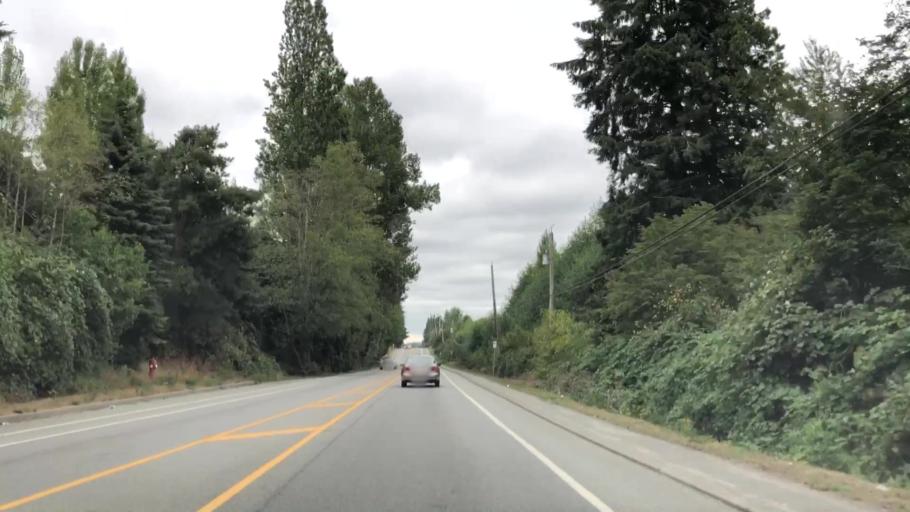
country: CA
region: British Columbia
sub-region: Greater Vancouver Regional District
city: White Rock
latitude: 49.0601
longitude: -122.7771
